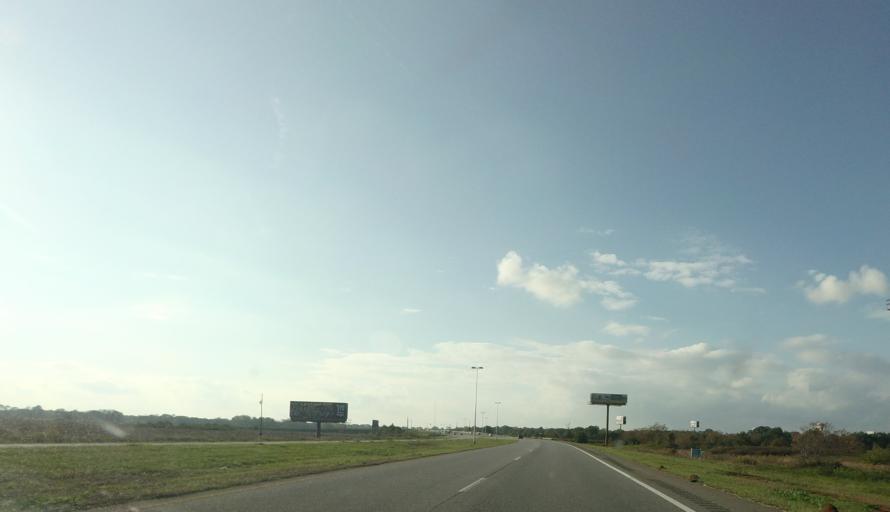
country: US
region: Georgia
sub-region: Houston County
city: Centerville
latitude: 32.5856
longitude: -83.7358
